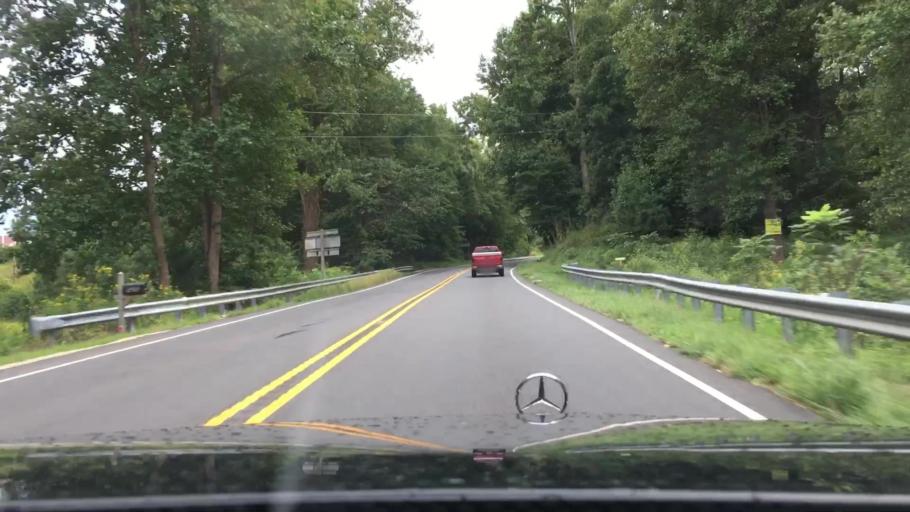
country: US
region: Virginia
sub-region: Nelson County
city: Nellysford
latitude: 37.9164
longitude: -78.8410
